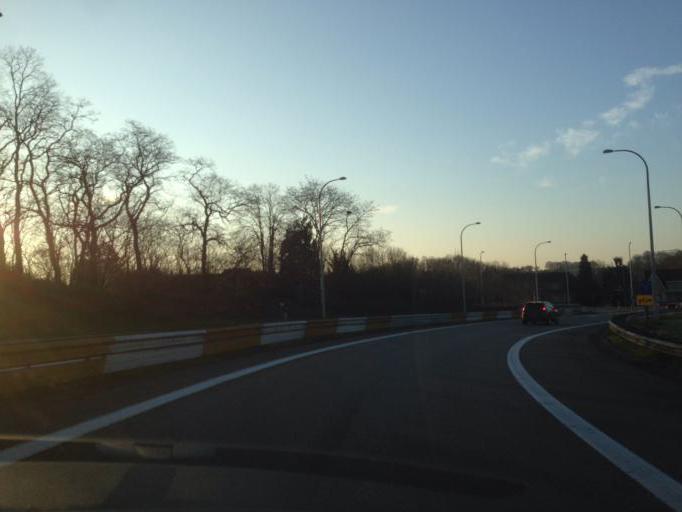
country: BE
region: Flanders
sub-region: Provincie Vlaams-Brabant
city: Bekkevoort
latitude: 50.9546
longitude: 5.0005
